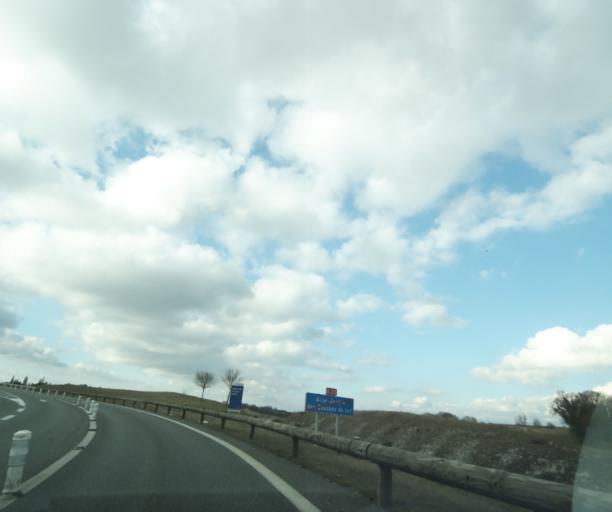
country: FR
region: Midi-Pyrenees
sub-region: Departement du Lot
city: Le Vigan
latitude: 44.6605
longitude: 1.5694
